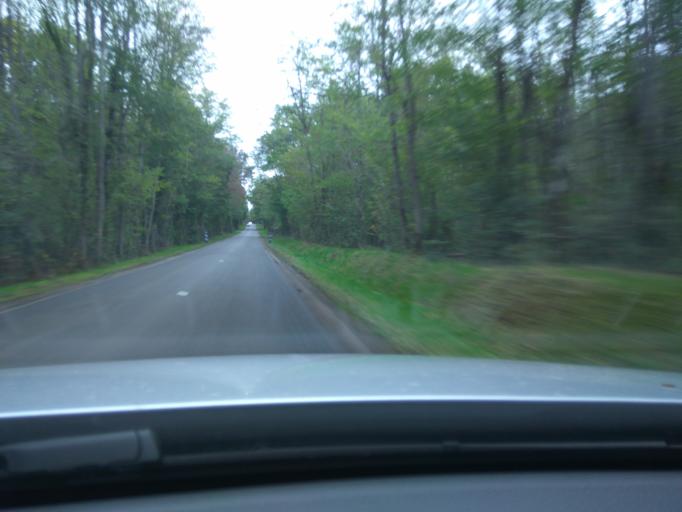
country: FR
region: Centre
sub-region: Departement du Cher
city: Saint-Satur
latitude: 47.3484
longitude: 2.8846
